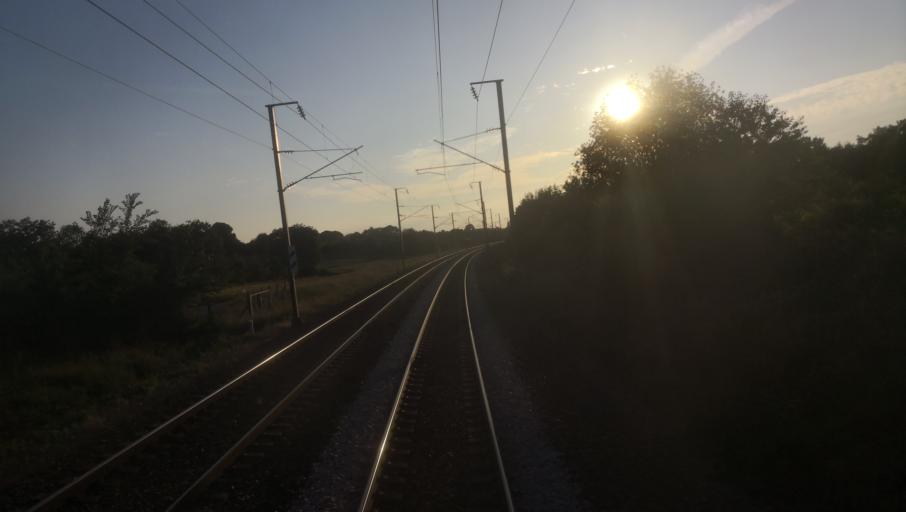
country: FR
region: Lower Normandy
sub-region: Departement du Calvados
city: La Vespiere
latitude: 49.0684
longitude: 0.4278
